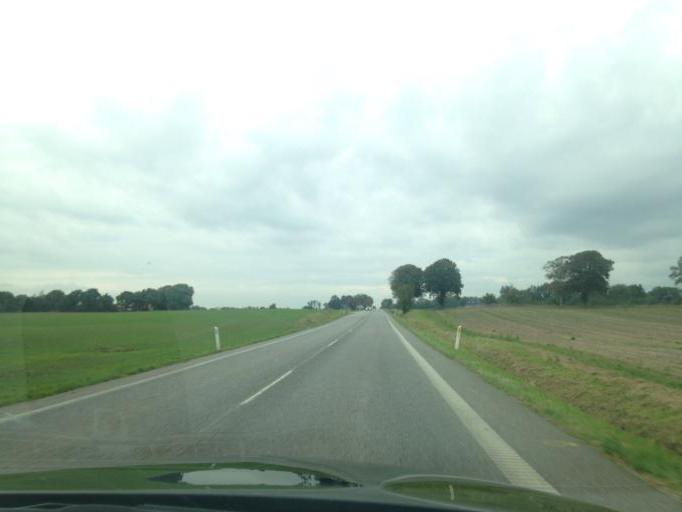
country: DK
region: South Denmark
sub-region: Kolding Kommune
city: Christiansfeld
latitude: 55.4183
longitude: 9.4769
